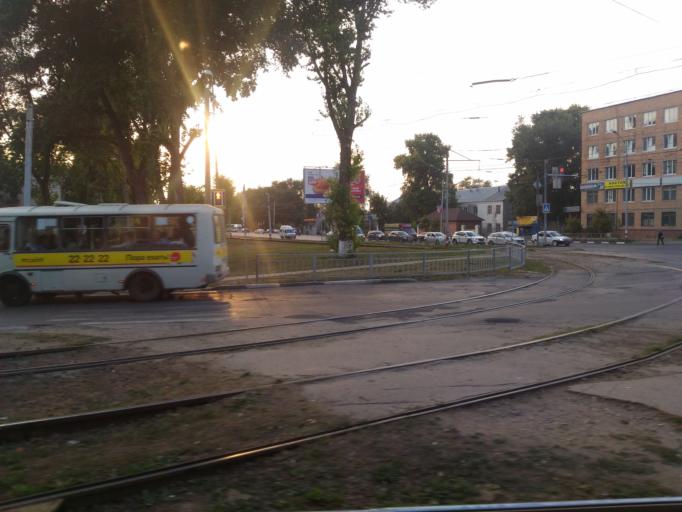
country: RU
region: Ulyanovsk
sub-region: Ulyanovskiy Rayon
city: Ulyanovsk
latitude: 54.3069
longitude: 48.3233
